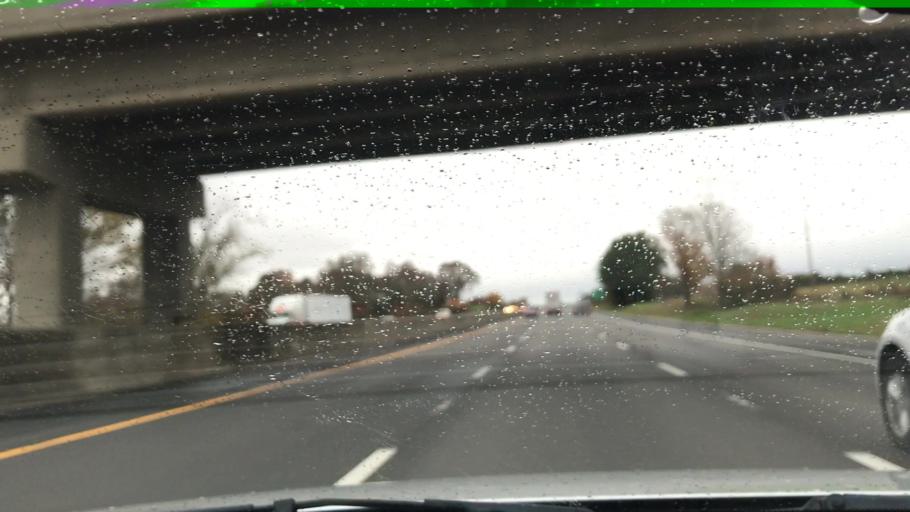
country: US
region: Kentucky
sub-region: Warren County
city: Bowling Green
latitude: 37.0126
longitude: -86.3069
